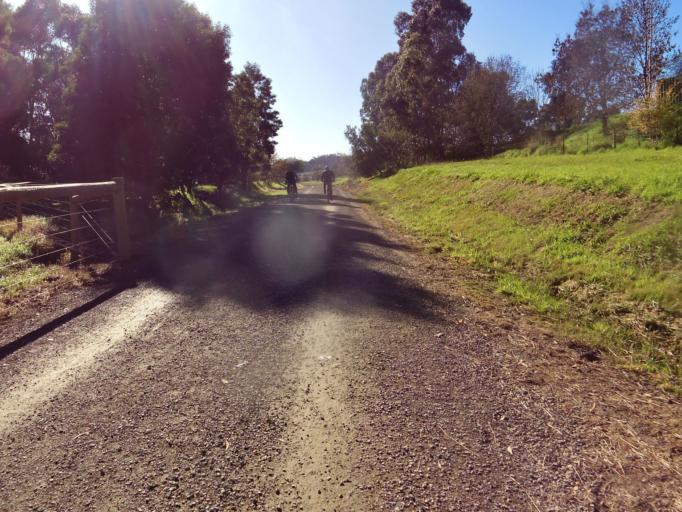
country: AU
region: Victoria
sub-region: Yarra Ranges
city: Lilydale
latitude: -37.7470
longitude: 145.3566
